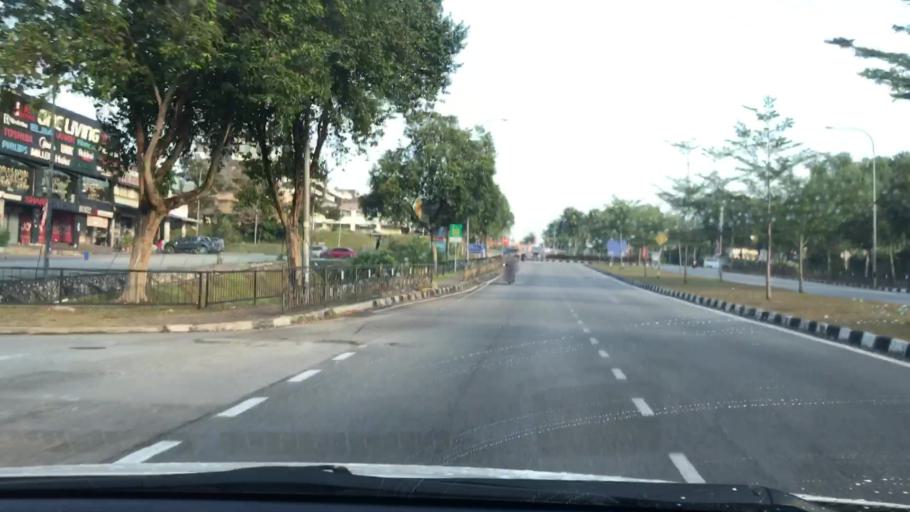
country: MY
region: Putrajaya
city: Putrajaya
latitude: 2.9934
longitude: 101.6741
